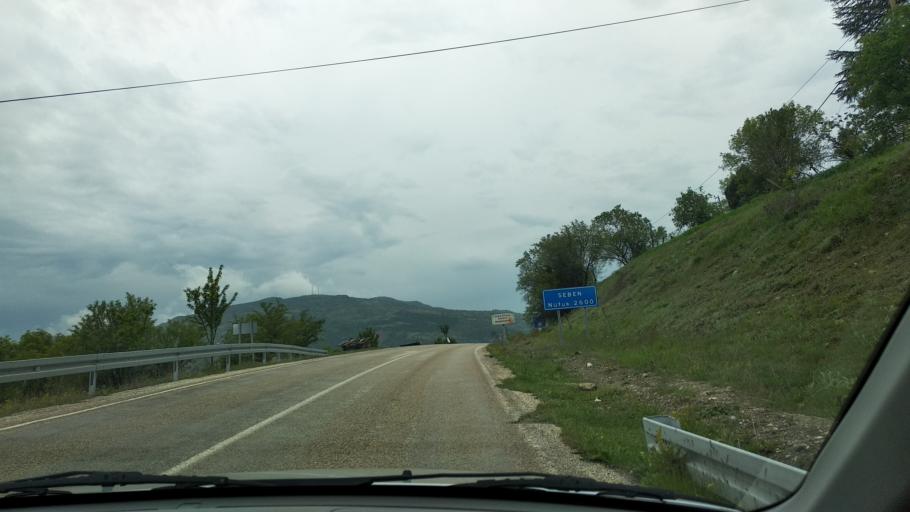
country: TR
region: Bolu
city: Seben
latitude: 40.4223
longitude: 31.5855
